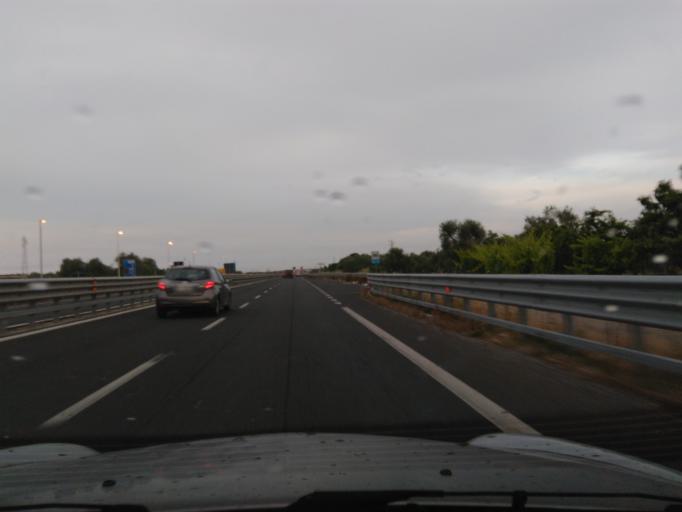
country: IT
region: Apulia
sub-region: Provincia di Bari
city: Giovinazzo
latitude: 41.1738
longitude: 16.6786
